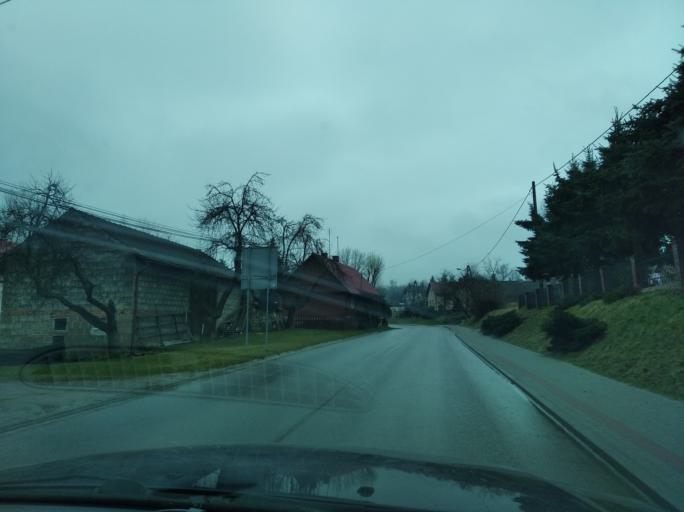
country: PL
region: Subcarpathian Voivodeship
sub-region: Powiat rzeszowski
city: Tyczyn
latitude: 49.9401
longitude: 22.0196
